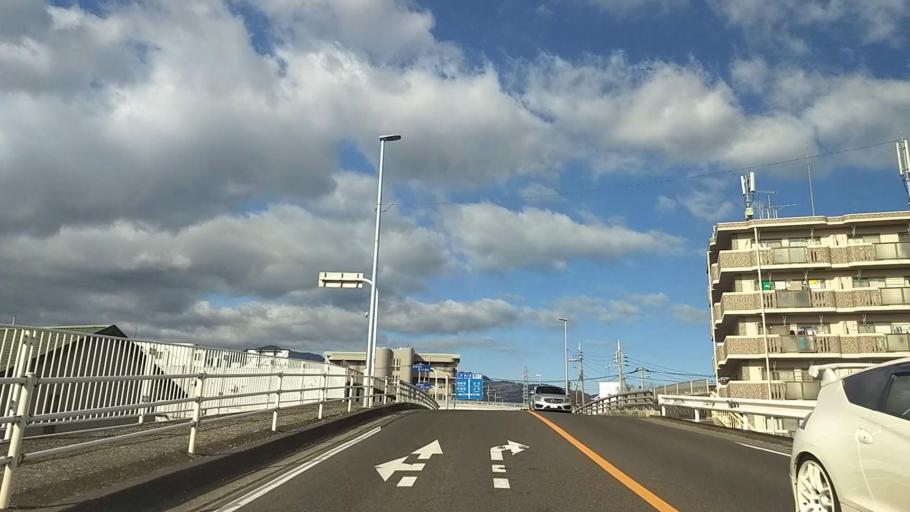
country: JP
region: Kanagawa
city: Atsugi
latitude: 35.4185
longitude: 139.3457
